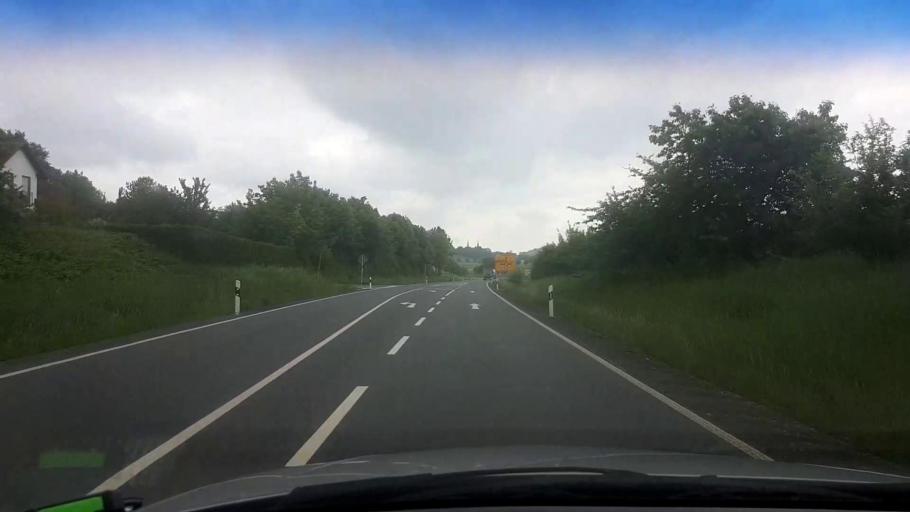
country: DE
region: Bavaria
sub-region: Upper Franconia
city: Goldkronach
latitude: 50.0067
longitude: 11.6785
